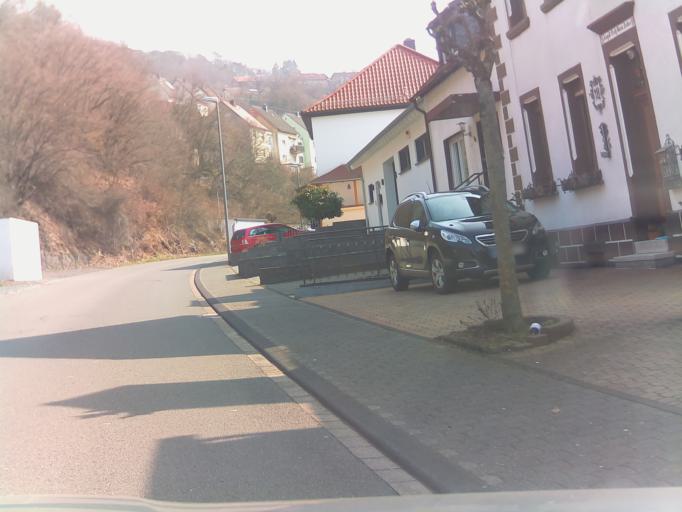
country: DE
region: Rheinland-Pfalz
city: Heimbach
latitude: 49.6127
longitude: 7.2507
